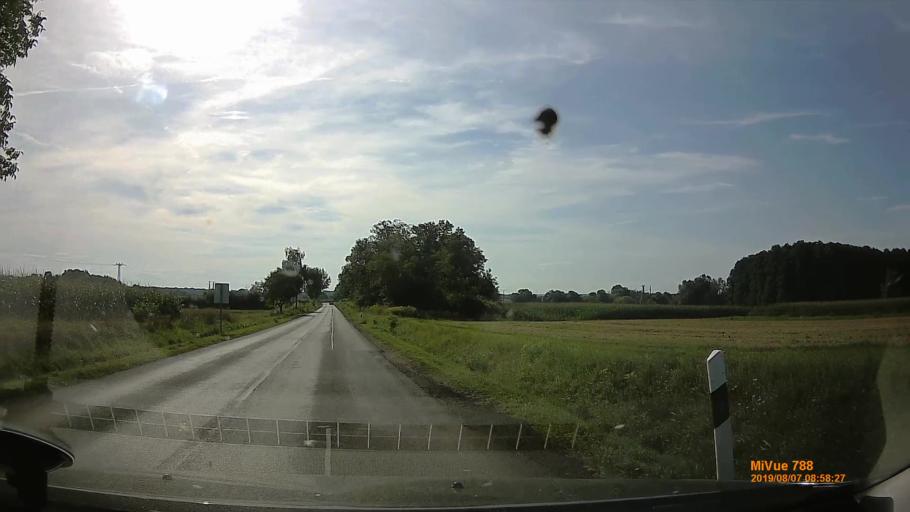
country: HU
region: Zala
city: Pacsa
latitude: 46.7431
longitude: 16.9241
